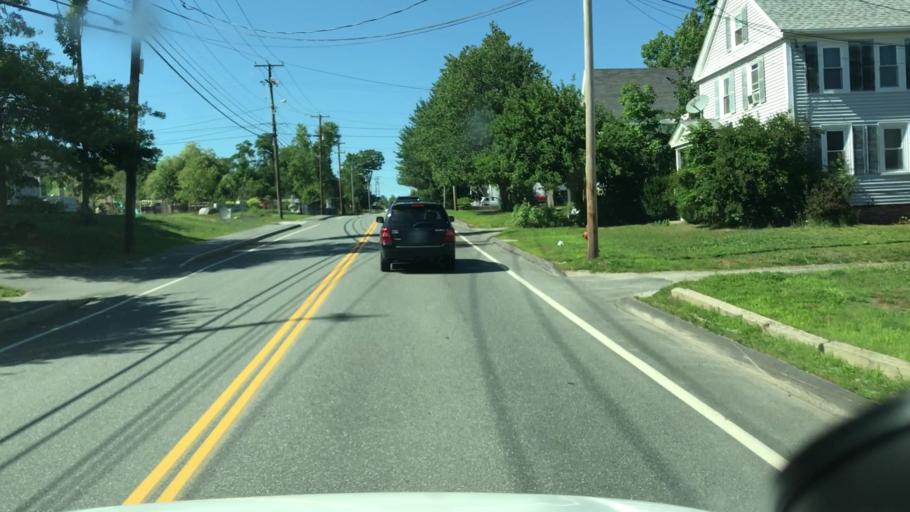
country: US
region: Maine
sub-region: Hancock County
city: Ellsworth
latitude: 44.5467
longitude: -68.4260
